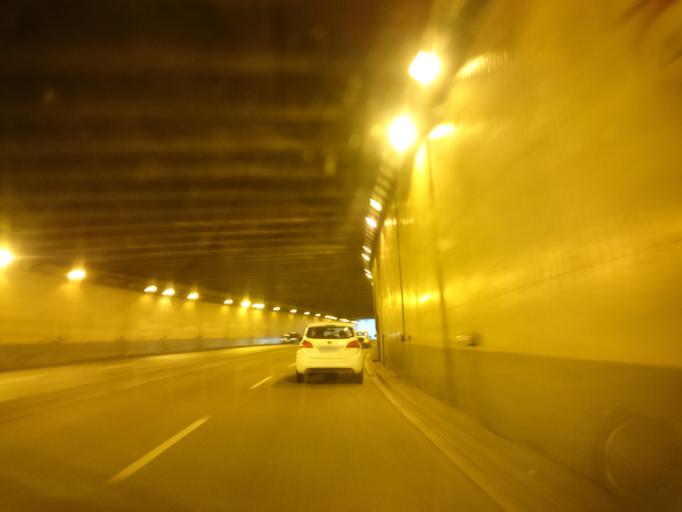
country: ES
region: Catalonia
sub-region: Provincia de Barcelona
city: Horta-Guinardo
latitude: 41.4286
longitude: 2.1572
